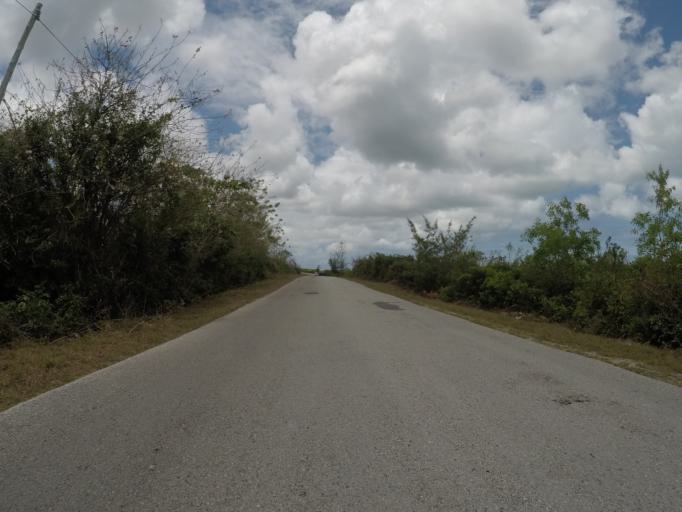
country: TZ
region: Zanzibar Central/South
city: Mahonda
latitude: -6.3299
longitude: 39.4378
